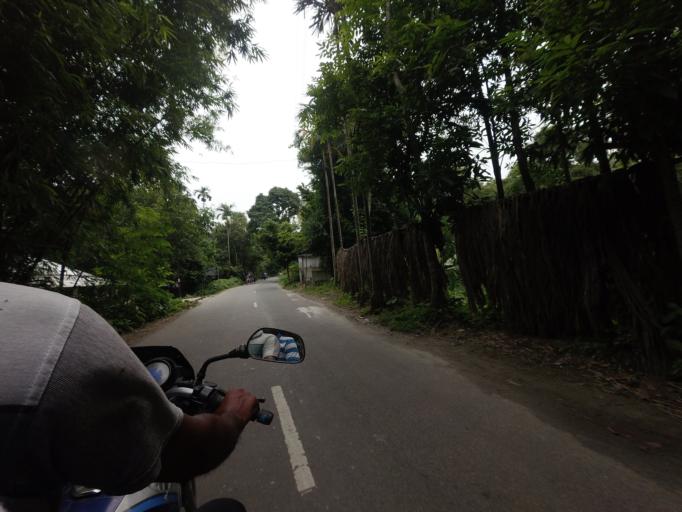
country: BD
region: Khulna
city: Kalia
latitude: 23.1683
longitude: 89.6455
